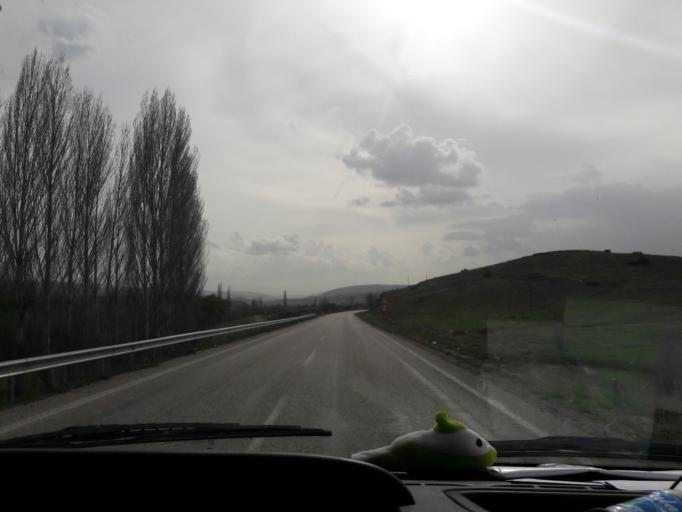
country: TR
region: Gumushane
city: Siran
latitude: 40.1634
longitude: 39.0435
